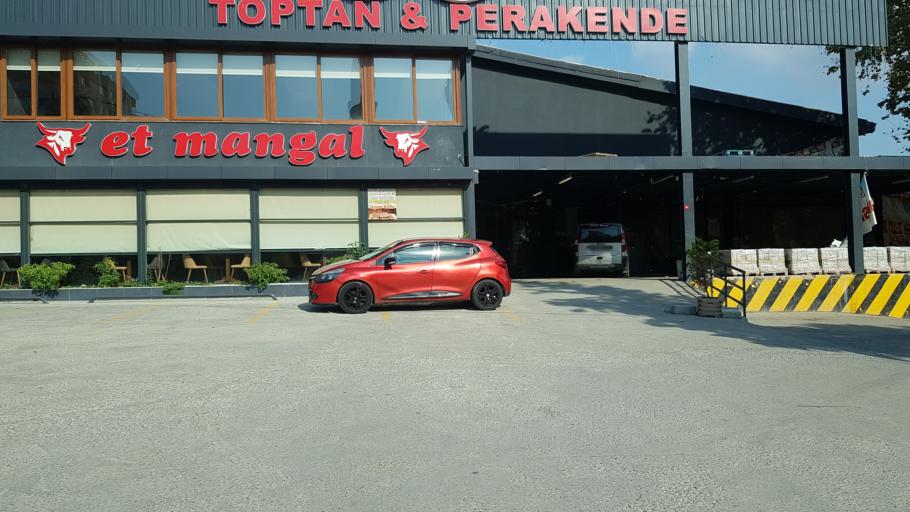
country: TR
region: Istanbul
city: Maltepe
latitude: 40.9041
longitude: 29.1964
